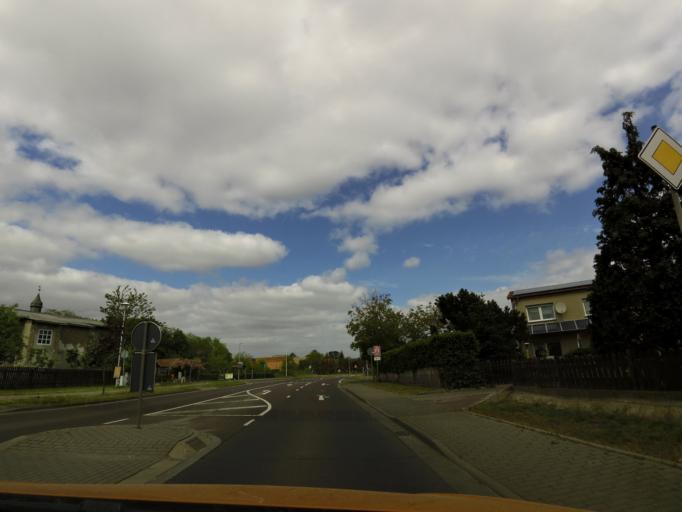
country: DE
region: Saxony-Anhalt
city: Mockern
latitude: 52.1895
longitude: 11.9091
